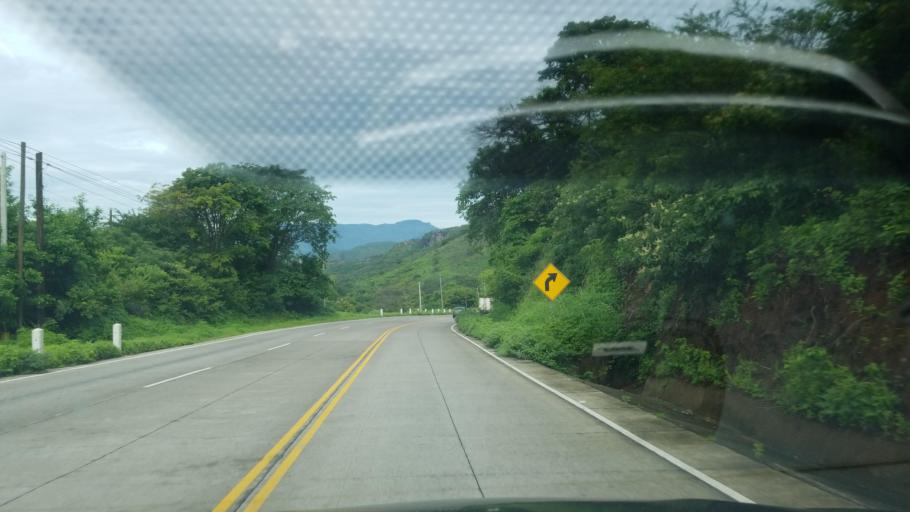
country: HN
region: Francisco Morazan
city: El Porvenir
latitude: 13.7000
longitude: -87.3172
